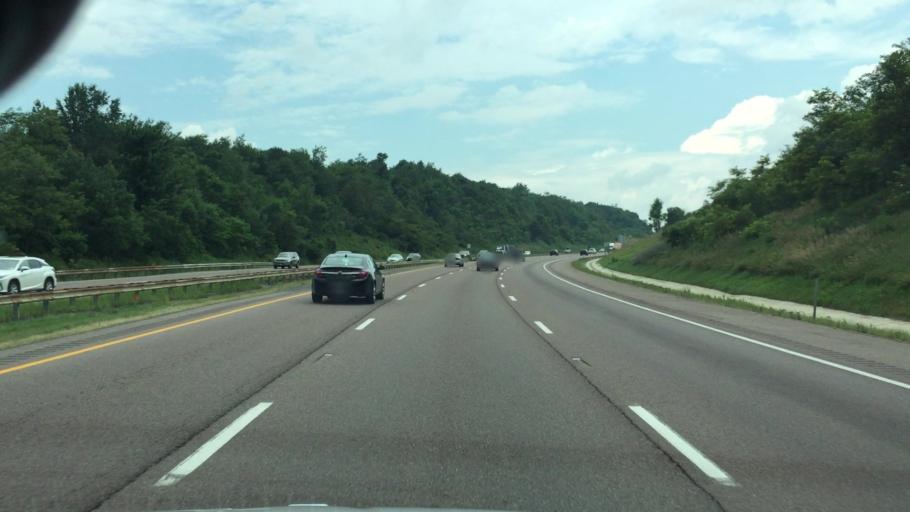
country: US
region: Maryland
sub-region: Allegany County
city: Frostburg
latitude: 39.6476
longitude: -78.9549
